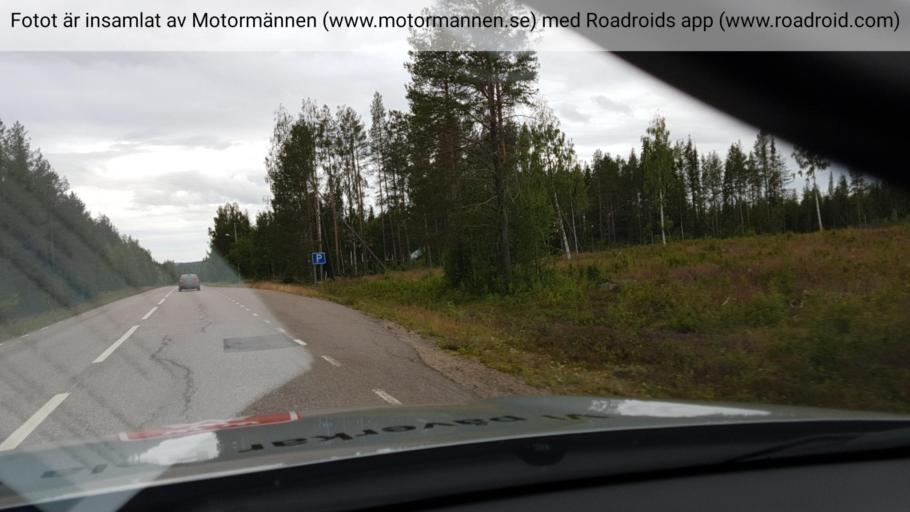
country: SE
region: Norrbotten
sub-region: Overkalix Kommun
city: OEverkalix
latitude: 66.6545
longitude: 22.8202
